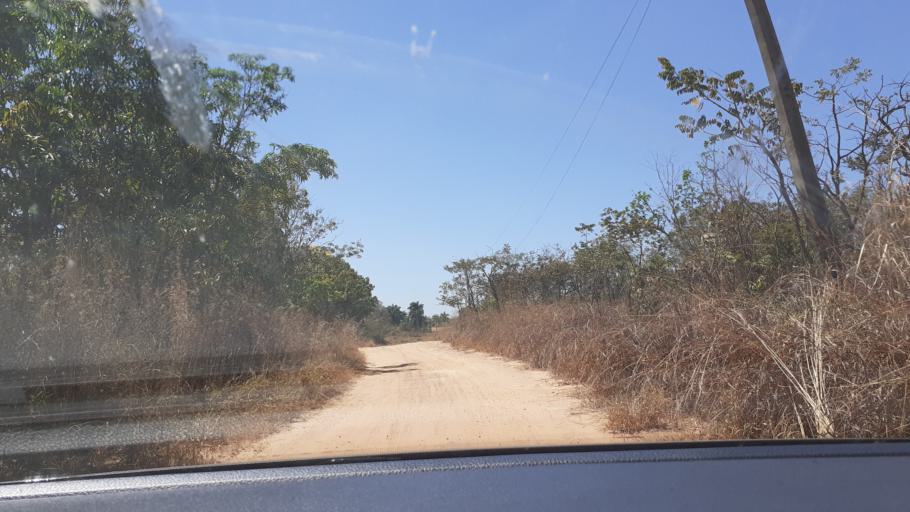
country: BR
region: Goias
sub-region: Caldas Novas
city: Caldas Novas
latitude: -17.7405
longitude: -48.6558
